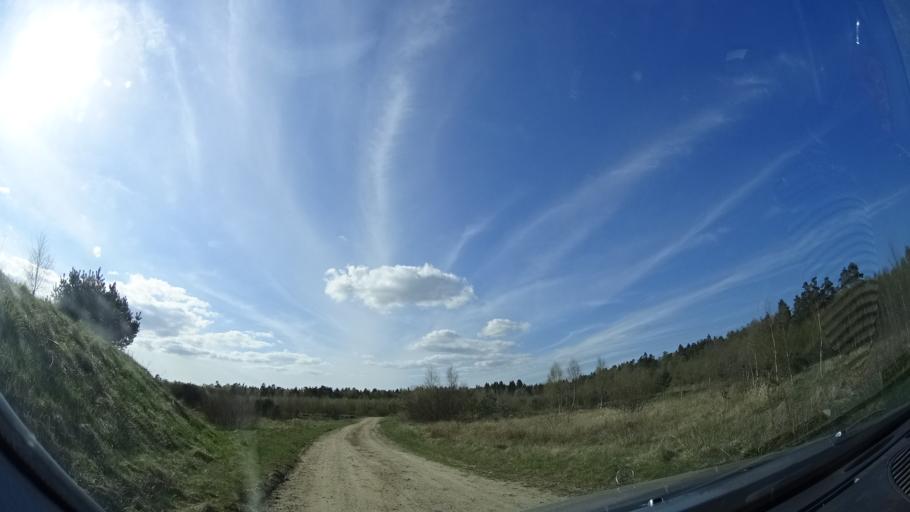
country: SE
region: Skane
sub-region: Hassleholms Kommun
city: Tormestorp
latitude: 56.1042
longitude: 13.6827
